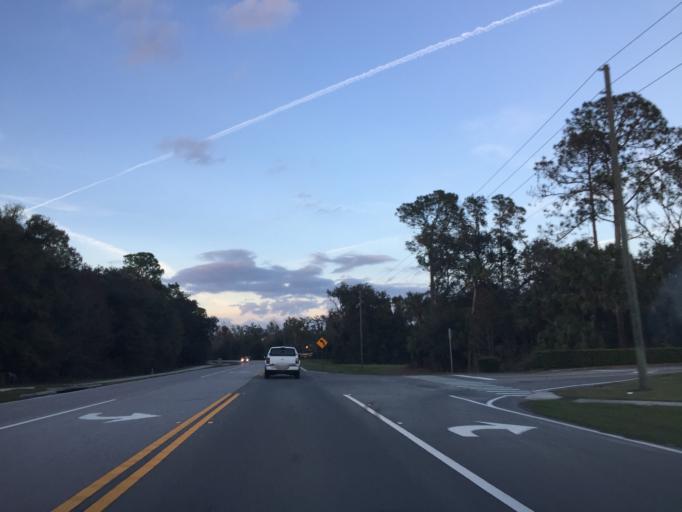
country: US
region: Florida
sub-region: Seminole County
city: Oviedo
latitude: 28.6709
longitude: -81.1761
